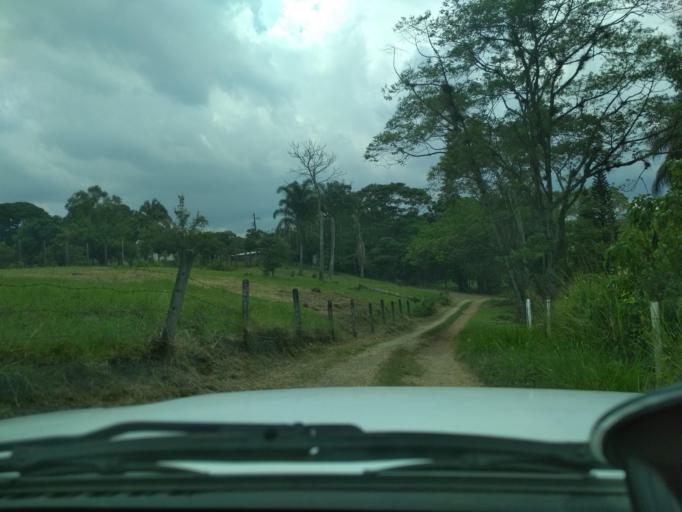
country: MX
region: Veracruz
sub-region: Cordoba
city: San Jose de Abajo [Unidad Habitacional]
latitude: 18.9188
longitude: -96.9557
